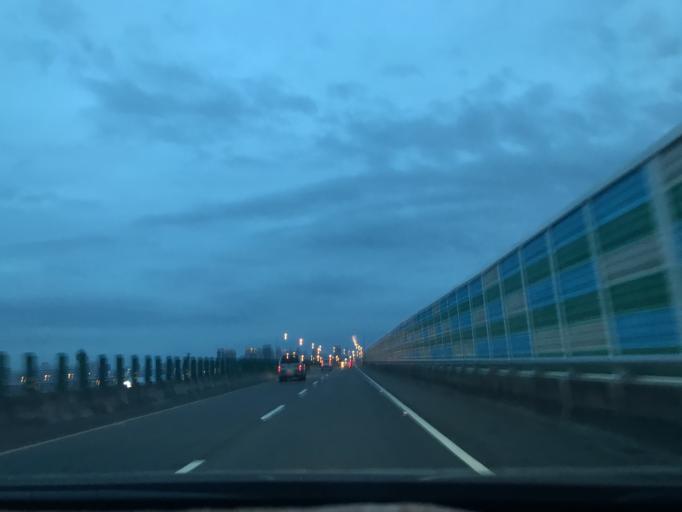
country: TW
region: Taiwan
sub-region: Hsinchu
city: Zhubei
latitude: 24.8218
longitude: 120.9883
